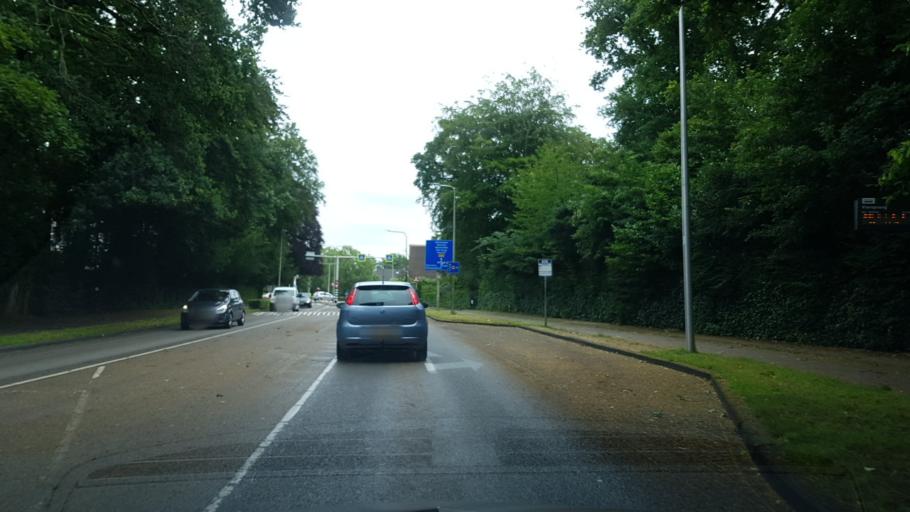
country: NL
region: North Holland
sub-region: Gemeente Heemstede
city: Heemstede
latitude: 52.3610
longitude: 4.5968
